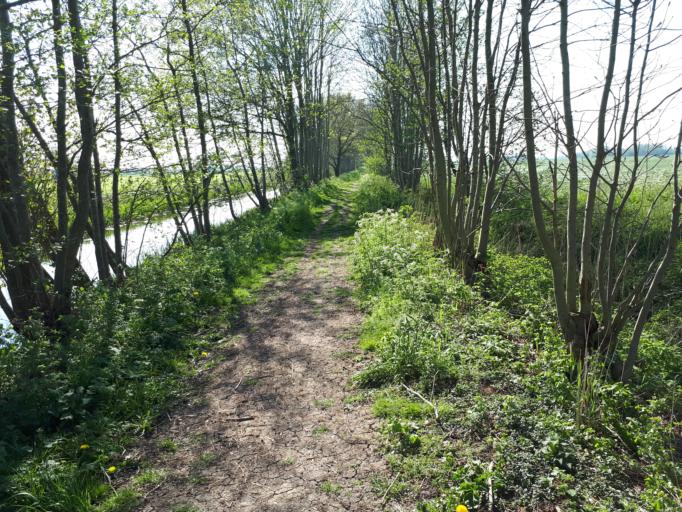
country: NL
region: Utrecht
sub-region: Gemeente IJsselstein
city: IJsselstein
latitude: 52.0235
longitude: 5.0062
